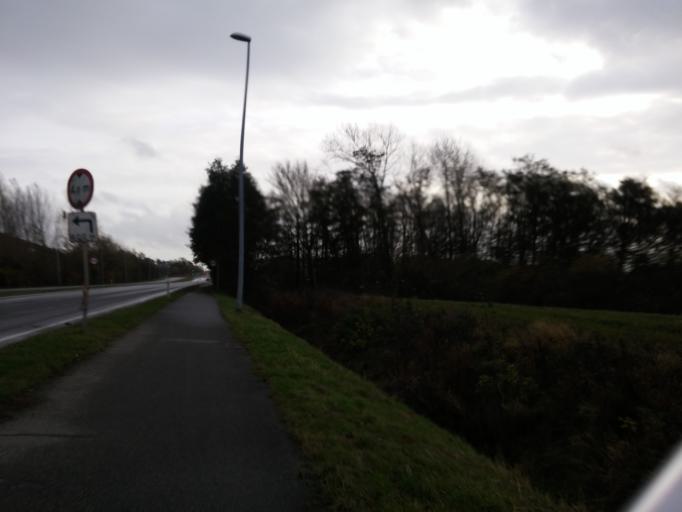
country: DK
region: South Denmark
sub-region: Kerteminde Kommune
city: Munkebo
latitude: 55.4553
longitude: 10.5374
